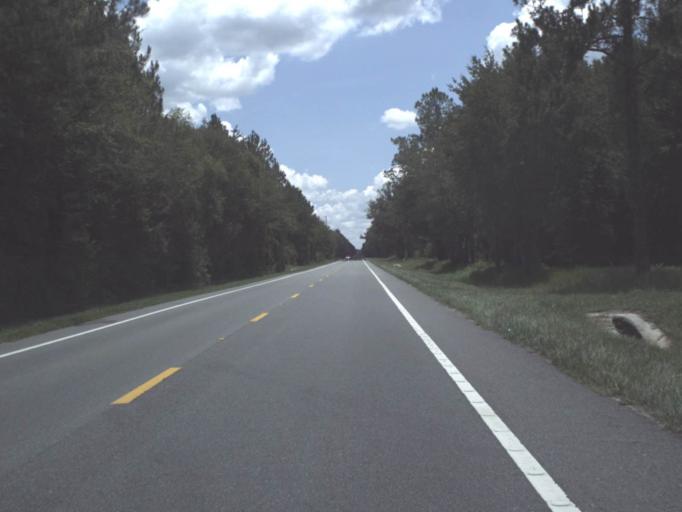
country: US
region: Florida
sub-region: Hamilton County
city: Jasper
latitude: 30.5856
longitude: -83.0027
